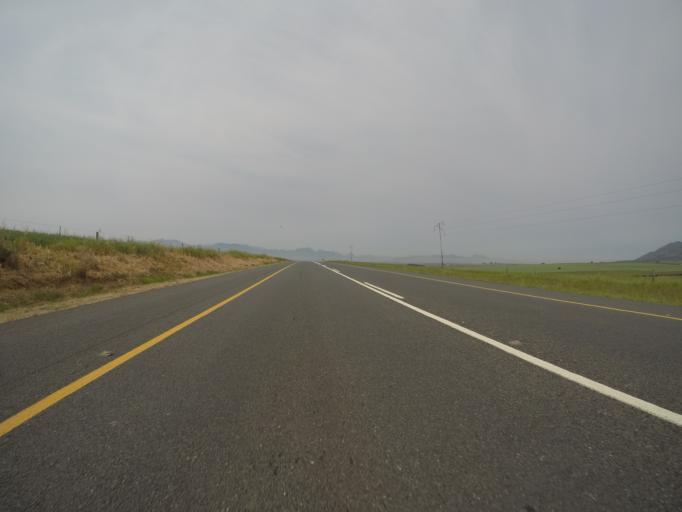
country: ZA
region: Western Cape
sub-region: West Coast District Municipality
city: Malmesbury
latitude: -33.5509
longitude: 18.8697
